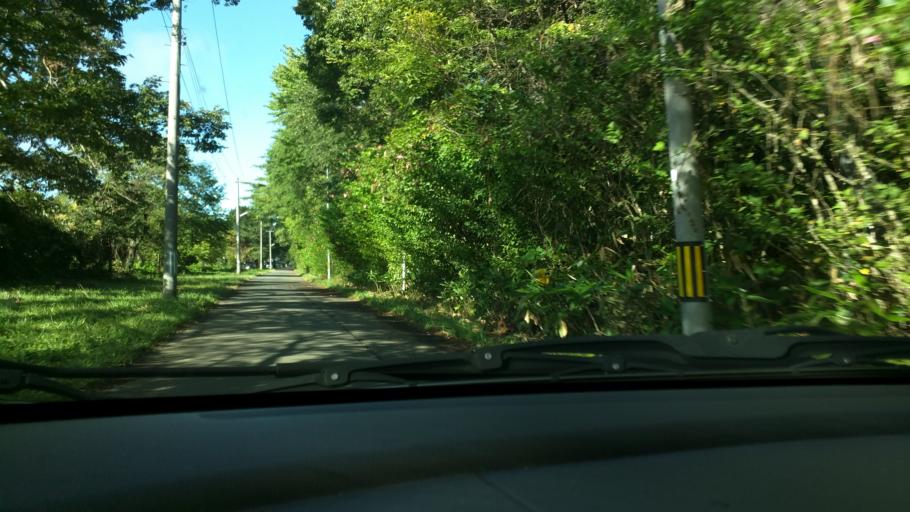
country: JP
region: Fukushima
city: Inawashiro
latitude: 37.4244
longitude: 140.1354
